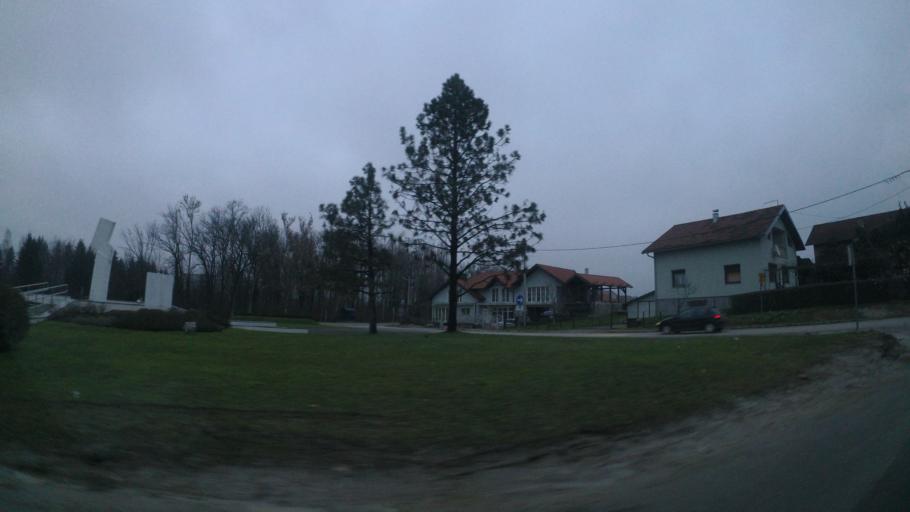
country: HR
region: Sisacko-Moslavacka
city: Petrinja
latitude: 45.4402
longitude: 16.2997
